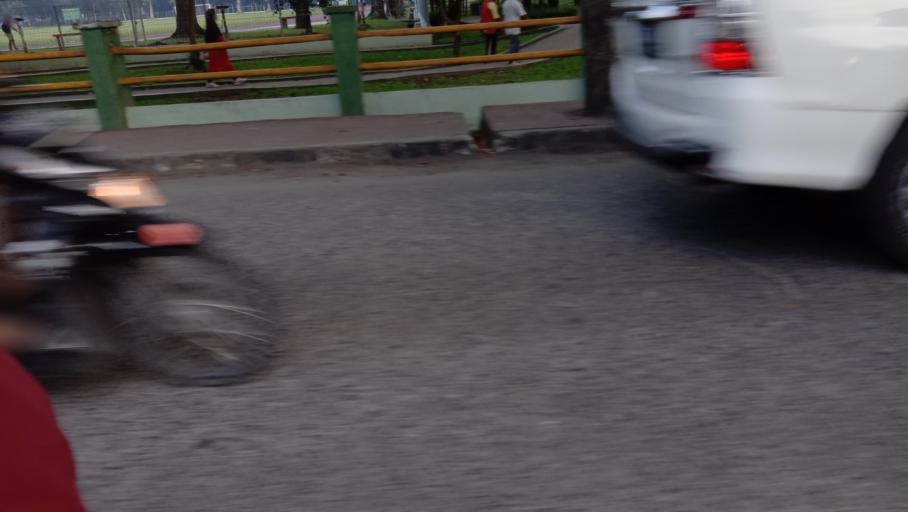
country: ID
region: North Sumatra
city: Medan
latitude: 3.6048
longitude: 98.6382
